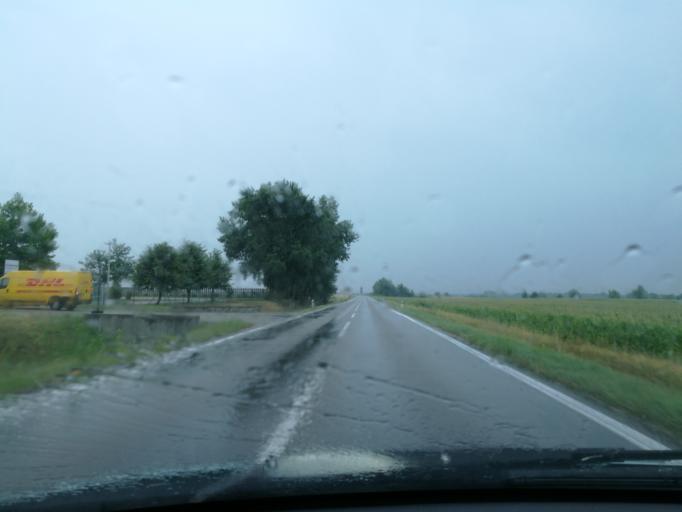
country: SK
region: Nitriansky
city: Komarno
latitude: 47.7659
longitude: 18.1614
